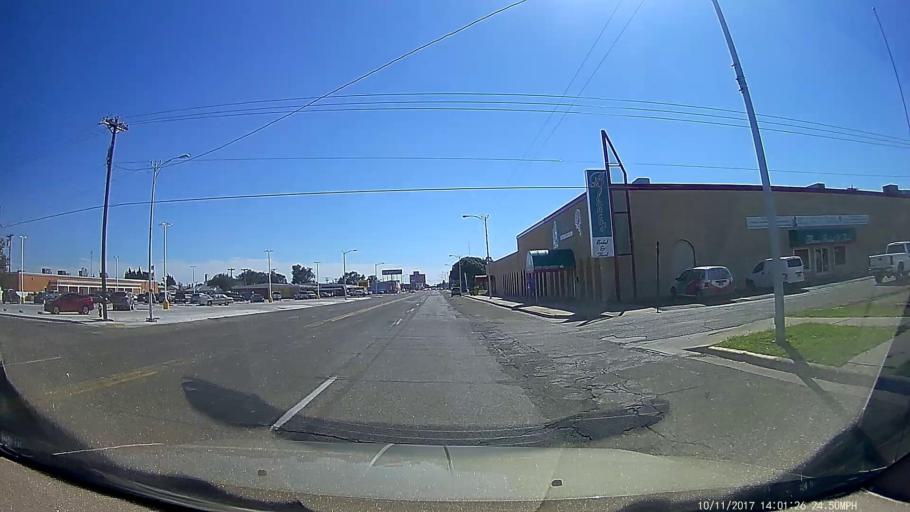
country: US
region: New Mexico
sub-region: Curry County
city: Clovis
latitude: 34.4090
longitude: -103.2054
